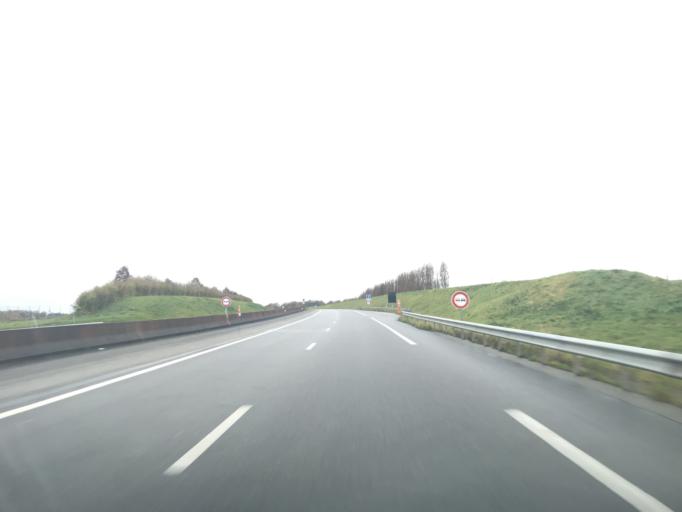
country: FR
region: Haute-Normandie
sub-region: Departement de l'Eure
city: Brionne
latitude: 49.2186
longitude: 0.7717
